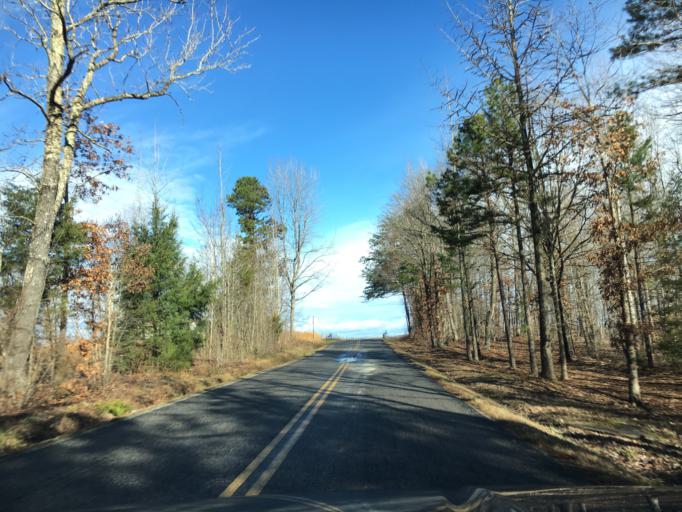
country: US
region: Virginia
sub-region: Amelia County
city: Amelia Court House
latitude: 37.4104
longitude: -78.0877
